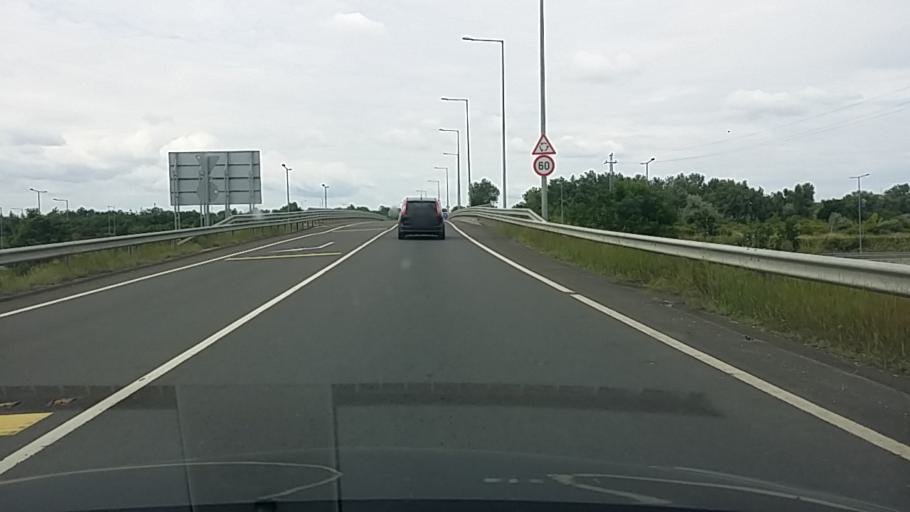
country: HU
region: Pest
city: Szada
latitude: 47.6131
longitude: 19.3261
